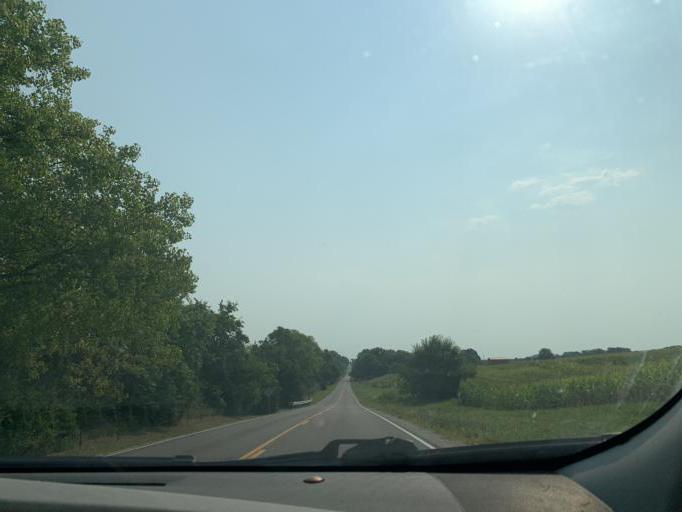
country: US
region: Illinois
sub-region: Whiteside County
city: Sterling
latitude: 41.8442
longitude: -89.8005
